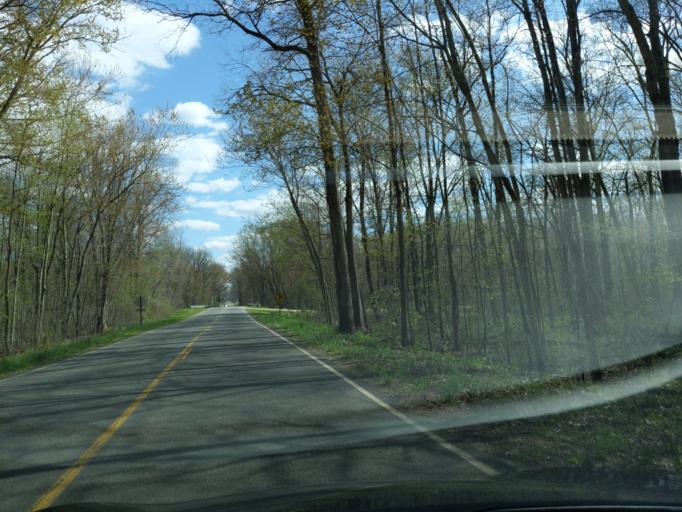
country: US
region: Michigan
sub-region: Ingham County
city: Leslie
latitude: 42.3924
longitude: -84.5416
